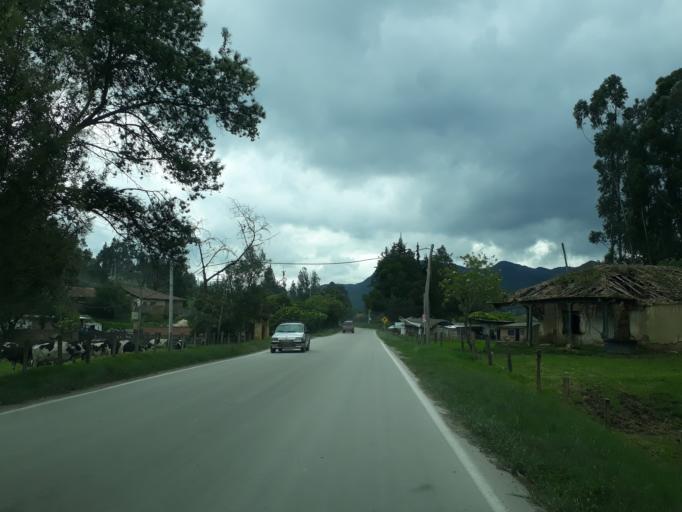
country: CO
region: Cundinamarca
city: Ubate
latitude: 5.3241
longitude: -73.7657
